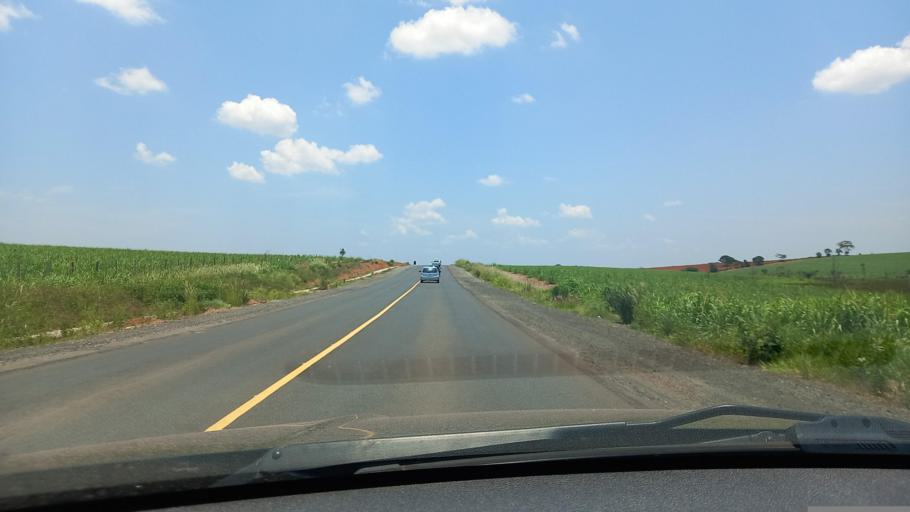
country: BR
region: Sao Paulo
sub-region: Moji-Guacu
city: Mogi-Gaucu
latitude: -22.3624
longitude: -46.8700
